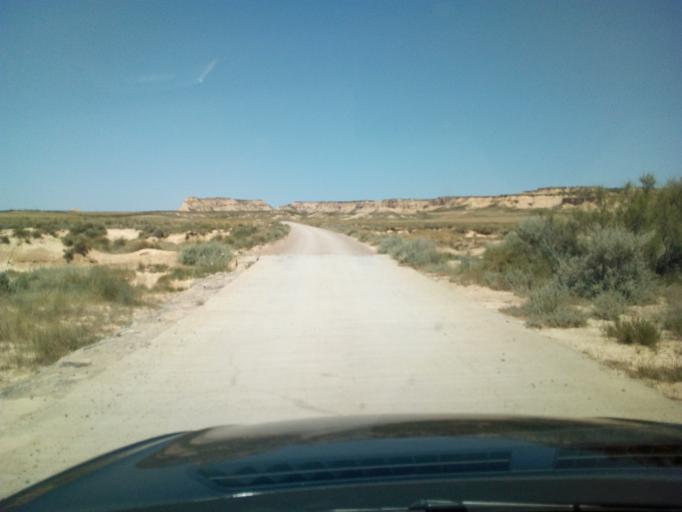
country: ES
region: Aragon
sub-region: Provincia de Zaragoza
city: Sadaba
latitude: 42.1837
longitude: -1.4099
